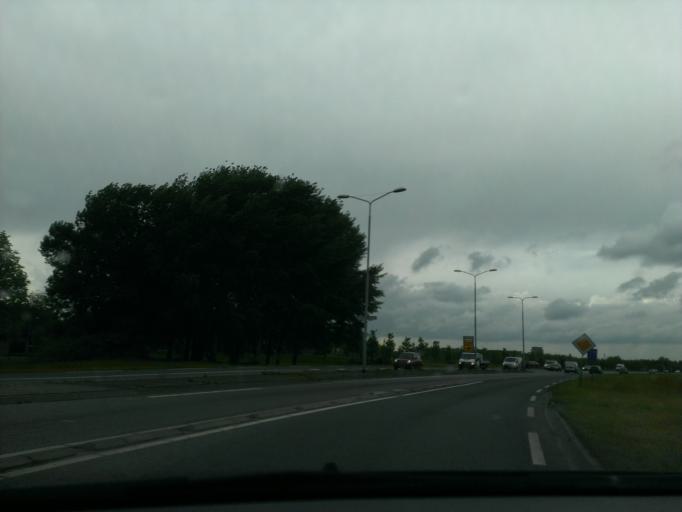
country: NL
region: Gelderland
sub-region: Gemeente Westervoort
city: Westervoort
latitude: 51.9487
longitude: 5.9342
